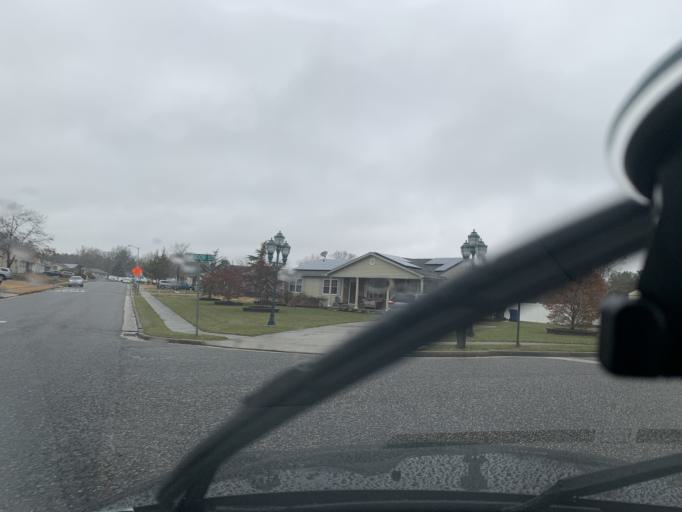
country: US
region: New Jersey
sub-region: Atlantic County
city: Pomona
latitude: 39.4318
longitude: -74.5931
